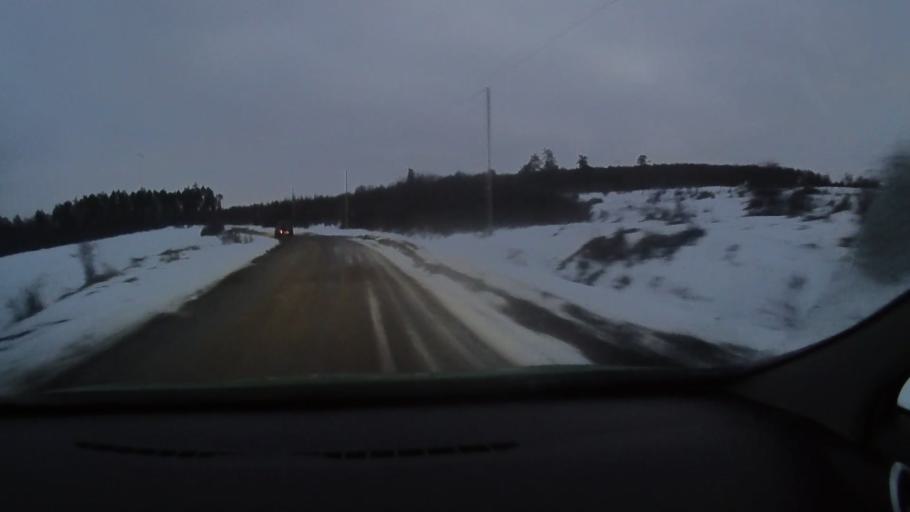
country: RO
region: Harghita
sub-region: Comuna Darjiu
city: Darjiu
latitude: 46.1854
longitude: 25.2476
